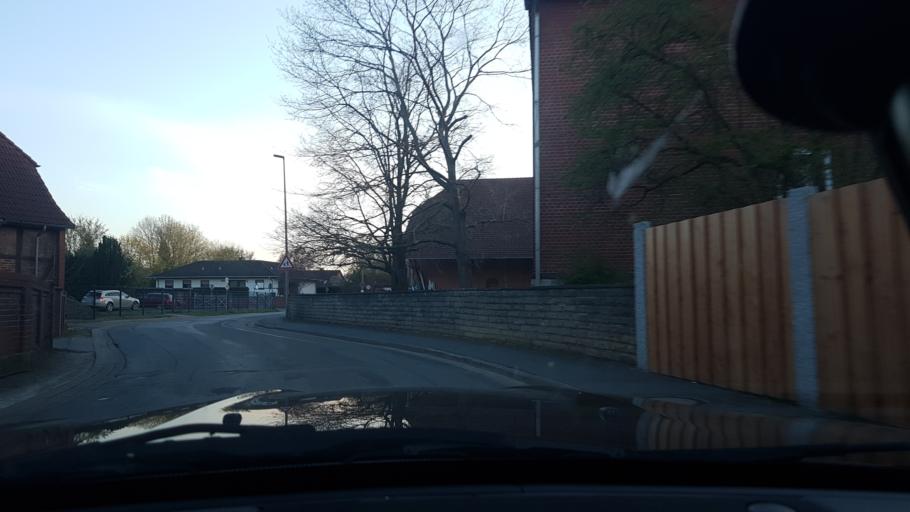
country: DE
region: Lower Saxony
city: Hemmingen
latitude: 52.2818
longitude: 9.7121
